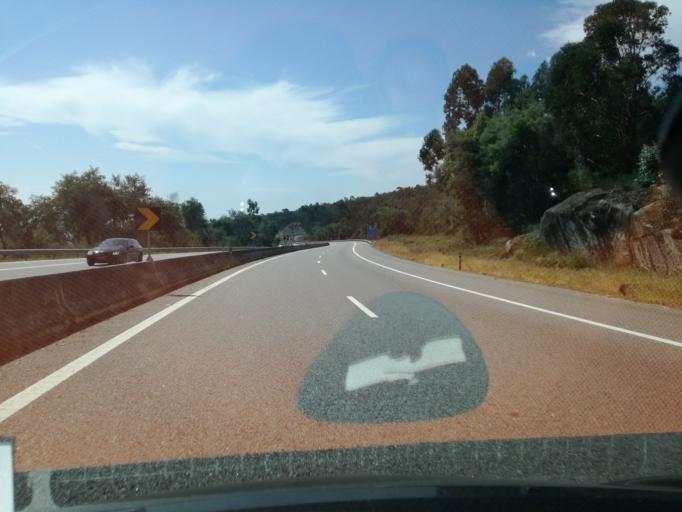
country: PT
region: Viana do Castelo
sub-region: Viana do Castelo
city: Meadela
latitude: 41.7368
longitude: -8.7915
